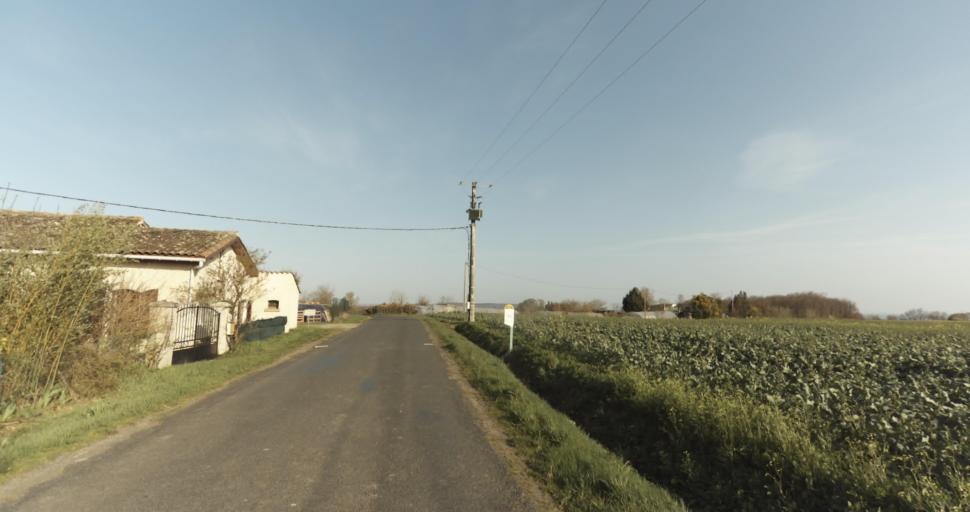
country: FR
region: Midi-Pyrenees
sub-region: Departement du Tarn
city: Saint-Sulpice-la-Pointe
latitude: 43.7340
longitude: 1.6939
